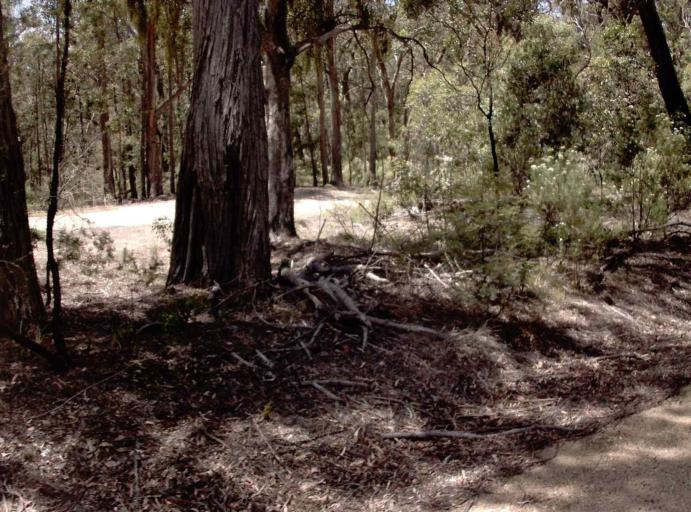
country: AU
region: Victoria
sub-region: East Gippsland
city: Lakes Entrance
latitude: -37.6344
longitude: 147.8960
